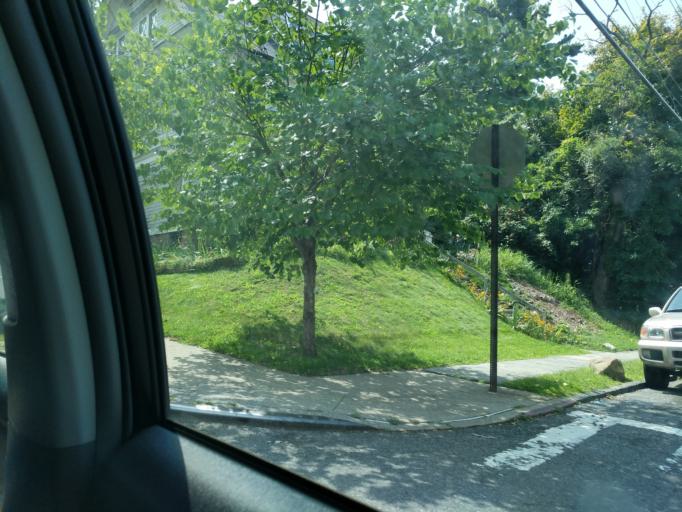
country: US
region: New Jersey
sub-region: Hudson County
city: Bayonne
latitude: 40.6393
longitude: -74.0939
